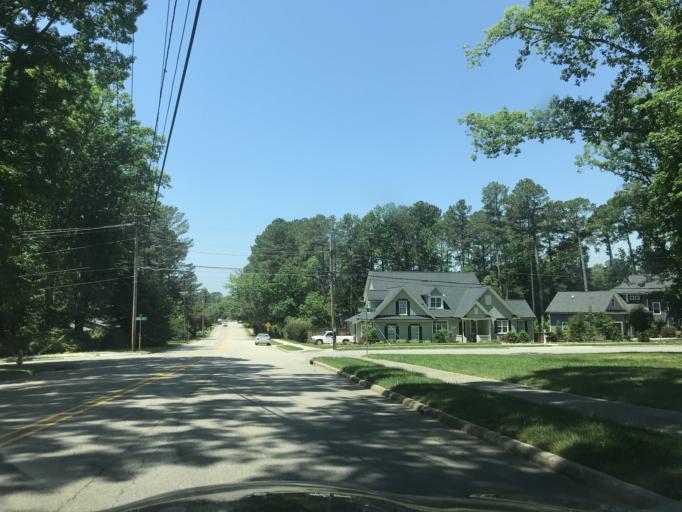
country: US
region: North Carolina
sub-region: Wake County
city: West Raleigh
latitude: 35.8527
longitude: -78.6543
